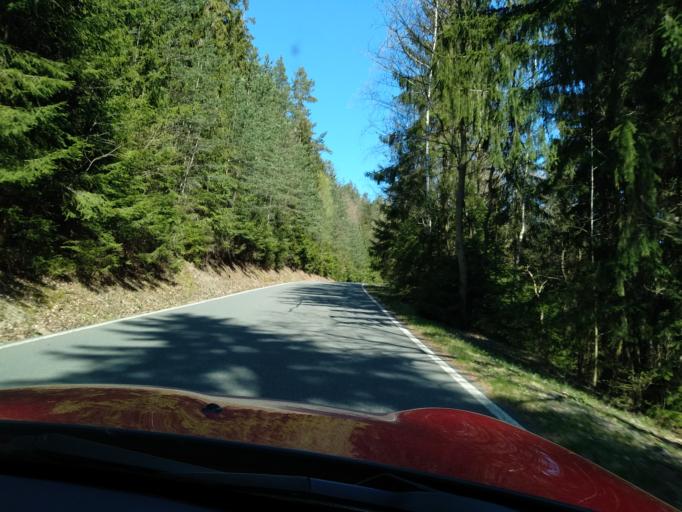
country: DE
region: Thuringia
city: Bad Blankenburg
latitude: 50.6461
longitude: 11.2821
